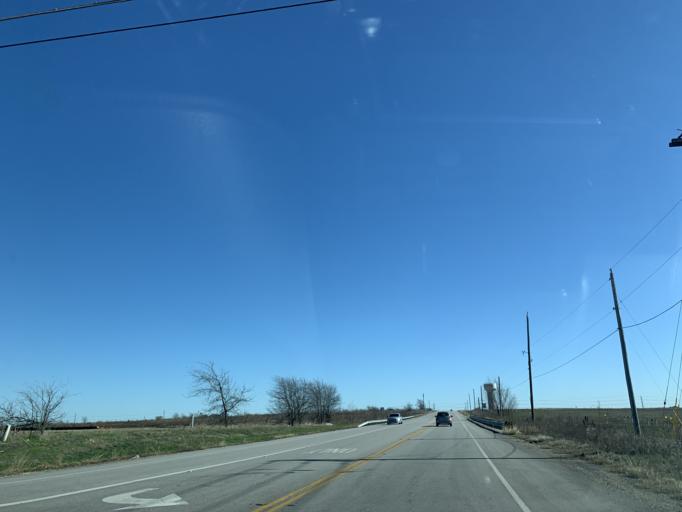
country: US
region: Texas
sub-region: Williamson County
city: Hutto
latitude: 30.5586
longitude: -97.5707
